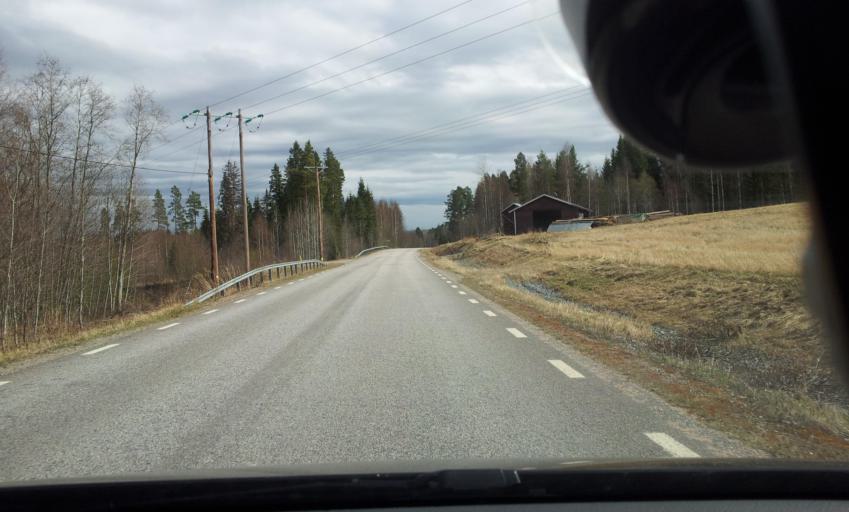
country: SE
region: Gaevleborg
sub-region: Ljusdals Kommun
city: Ljusdal
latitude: 61.7687
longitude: 16.0204
